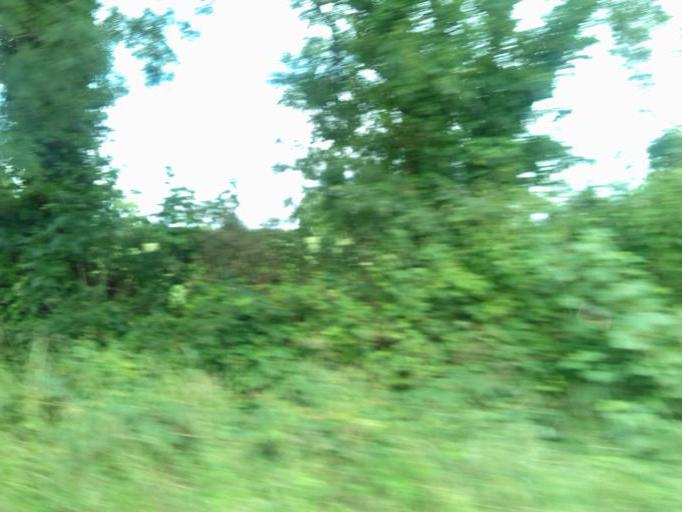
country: IE
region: Leinster
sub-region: Loch Garman
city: Enniscorthy
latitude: 52.4973
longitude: -6.5160
